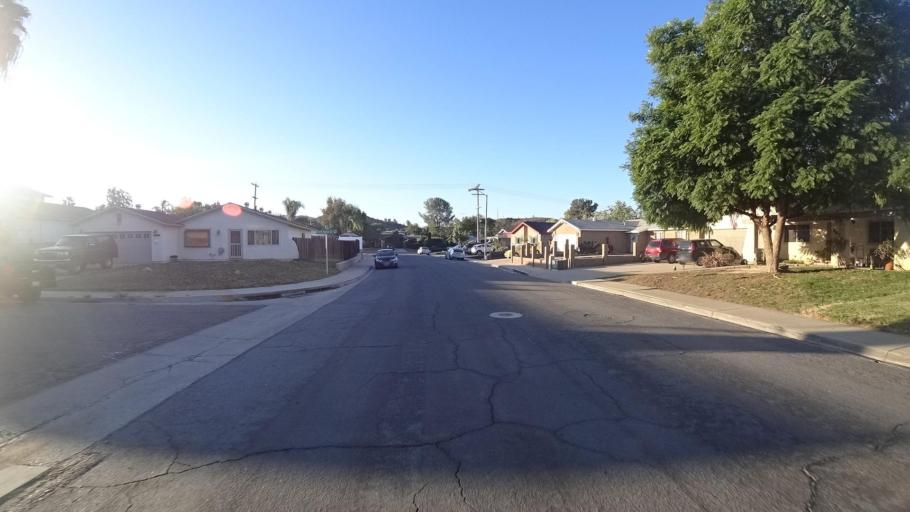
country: US
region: California
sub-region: San Diego County
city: Lakeside
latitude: 32.8605
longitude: -116.9033
